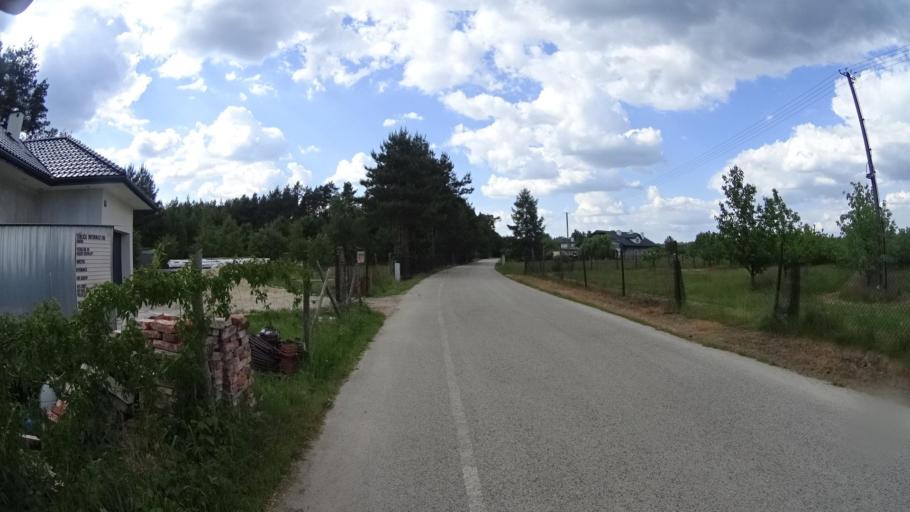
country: PL
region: Masovian Voivodeship
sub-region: Powiat piaseczynski
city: Tarczyn
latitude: 51.9980
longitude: 20.8352
